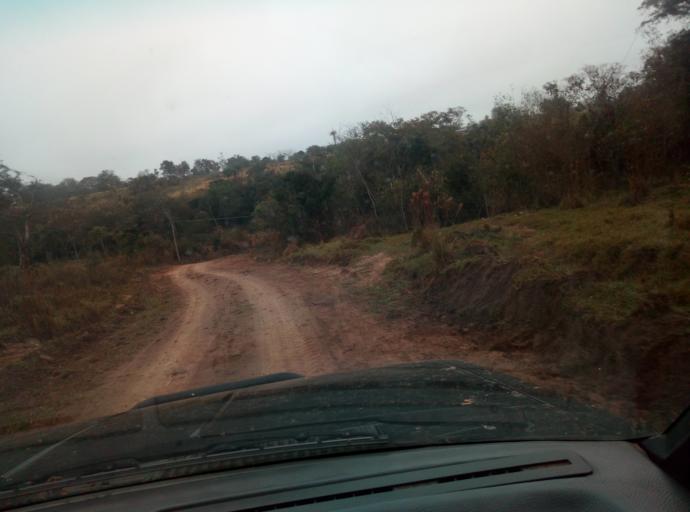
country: PY
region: Caaguazu
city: Carayao
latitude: -25.1936
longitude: -56.3219
